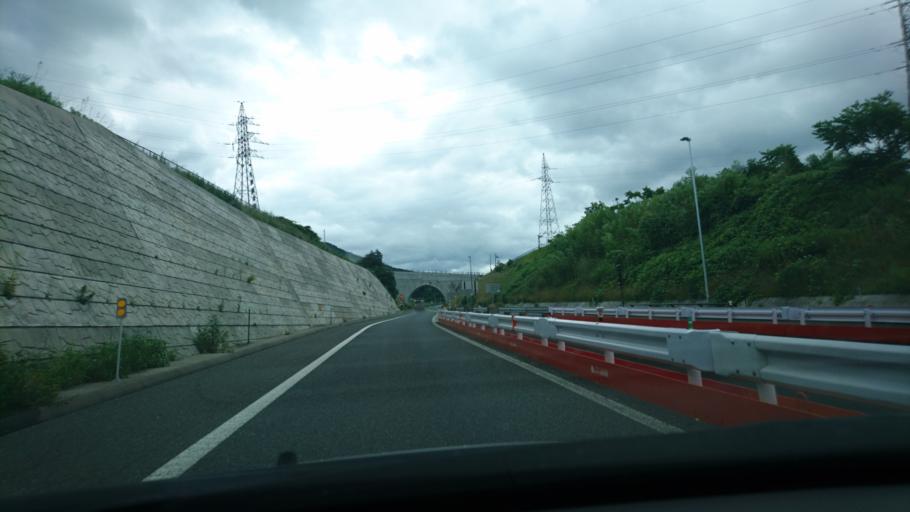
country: JP
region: Iwate
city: Ofunato
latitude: 39.0316
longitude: 141.6329
